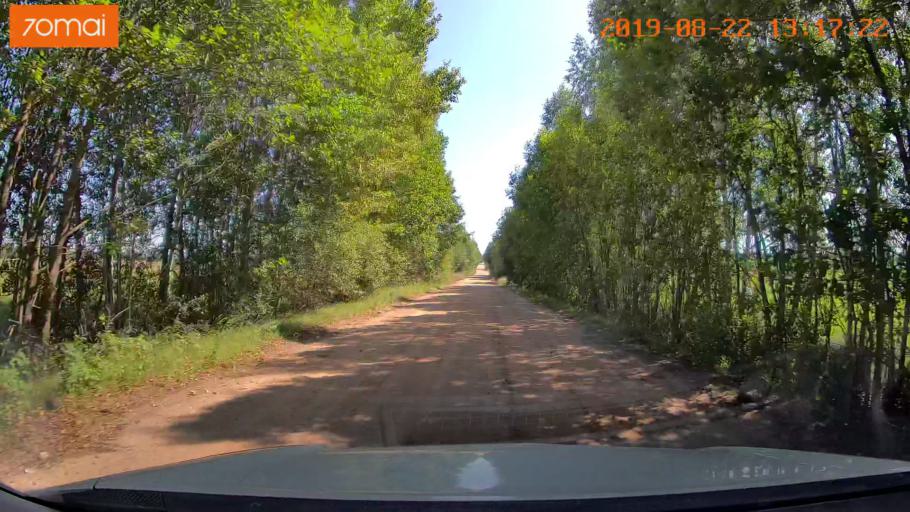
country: BY
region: Minsk
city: Prawdzinski
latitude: 53.2488
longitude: 27.9211
